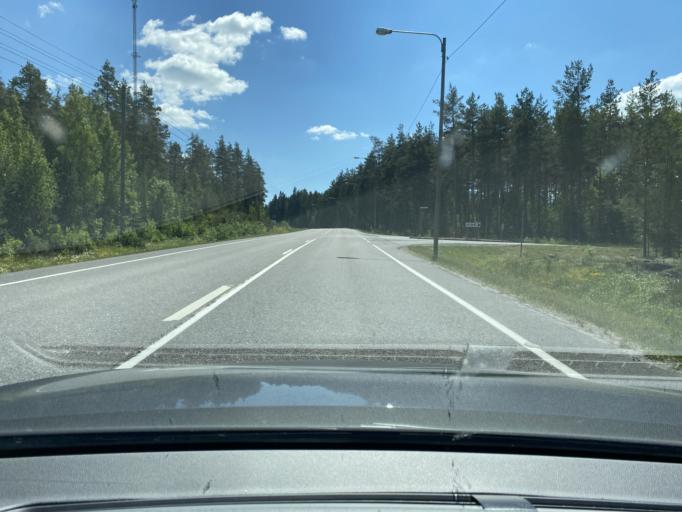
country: FI
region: Satakunta
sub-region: Rauma
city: Eura
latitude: 61.1325
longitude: 22.1728
